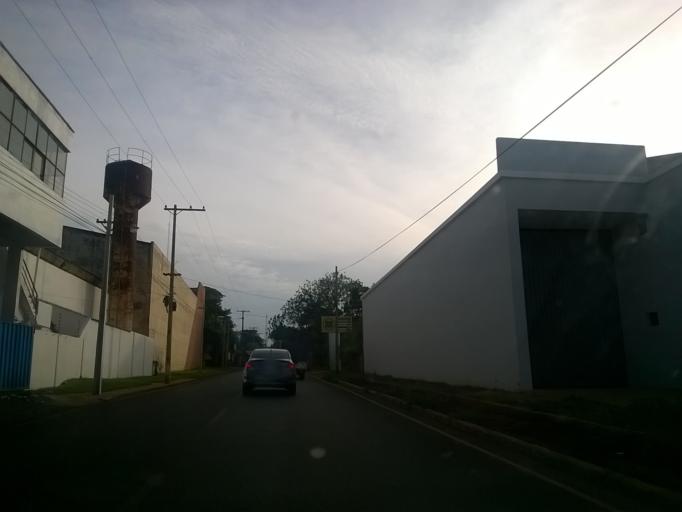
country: PY
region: Alto Parana
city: Ciudad del Este
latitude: -25.4997
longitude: -54.6332
